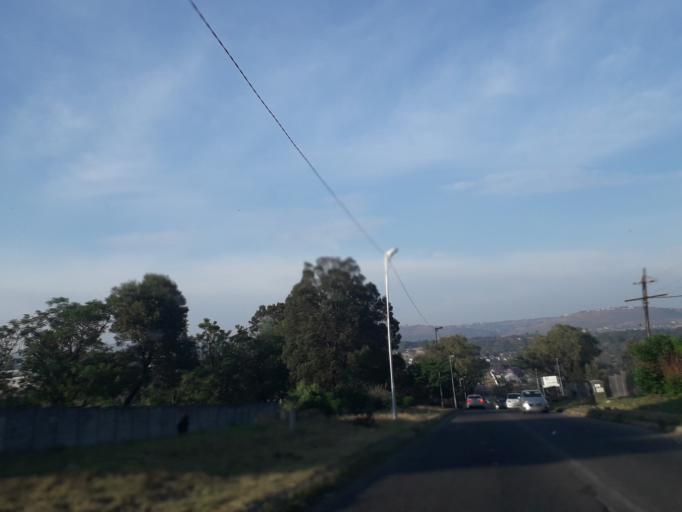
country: ZA
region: Gauteng
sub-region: West Rand District Municipality
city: Muldersdriseloop
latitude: -26.0757
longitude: 27.9108
